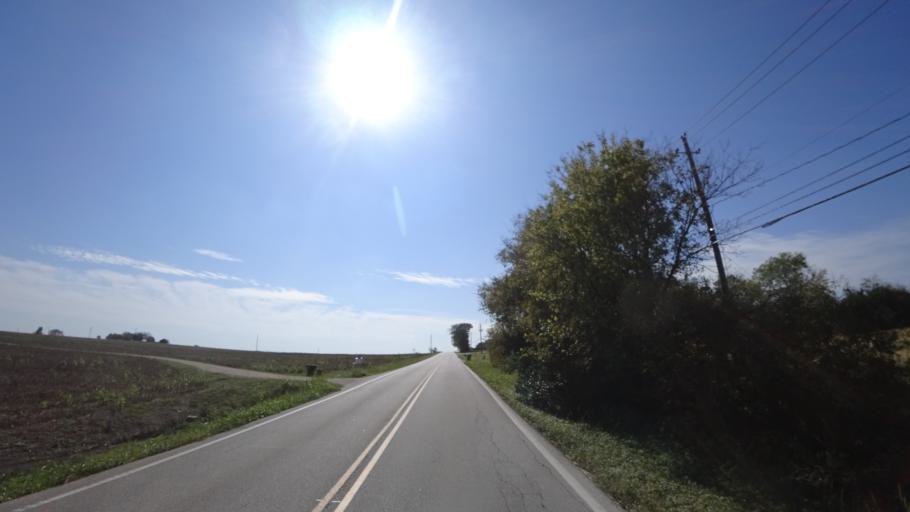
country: US
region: Texas
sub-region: Travis County
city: Pflugerville
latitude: 30.4162
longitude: -97.6226
